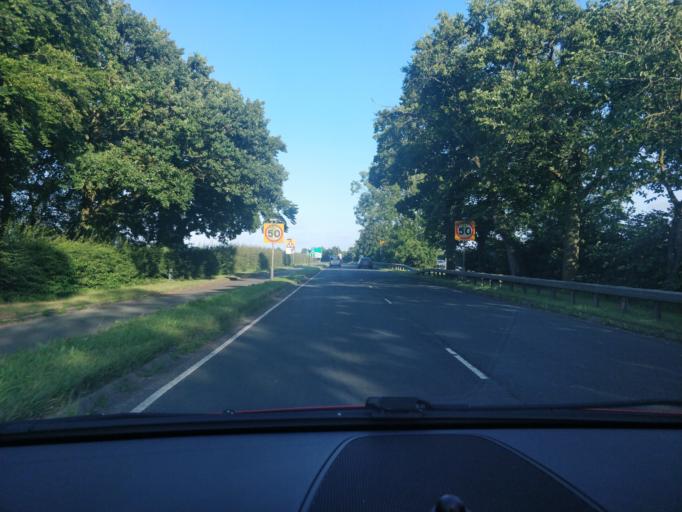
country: GB
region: England
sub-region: Lancashire
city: Banks
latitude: 53.6650
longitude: -2.8951
